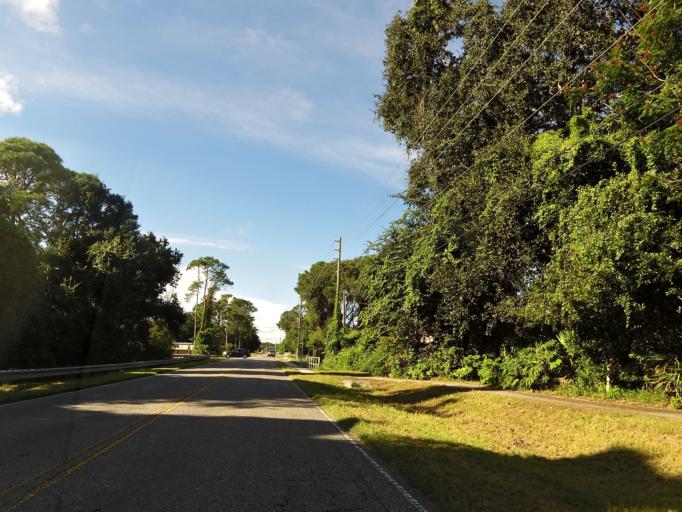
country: US
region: Florida
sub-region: Nassau County
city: Fernandina Beach
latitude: 30.6344
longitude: -81.4556
